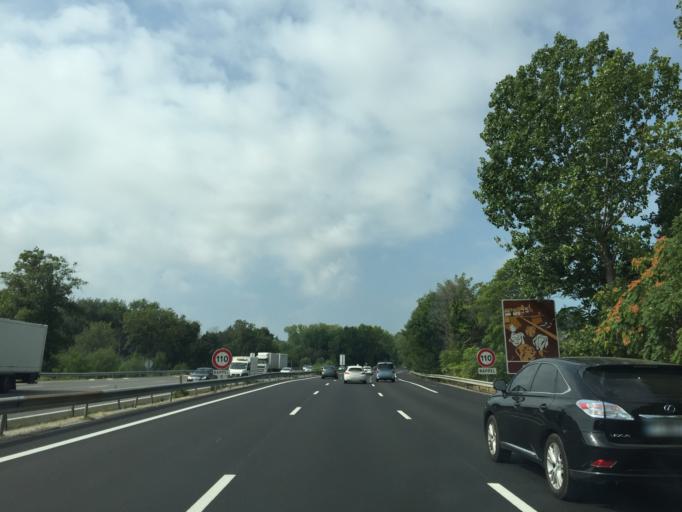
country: FR
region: Provence-Alpes-Cote d'Azur
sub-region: Departement des Alpes-Maritimes
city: Biot
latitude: 43.6156
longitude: 7.1144
